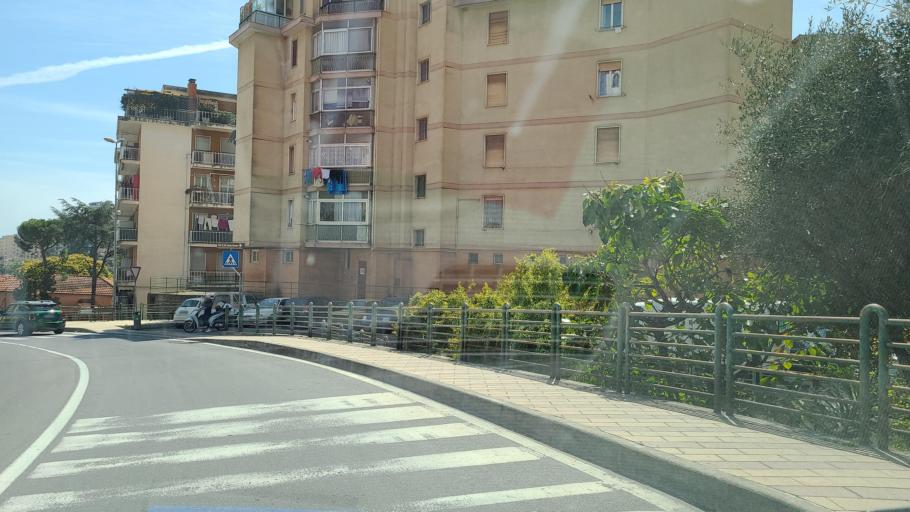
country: IT
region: Liguria
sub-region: Provincia di Imperia
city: San Remo
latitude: 43.8251
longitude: 7.7627
